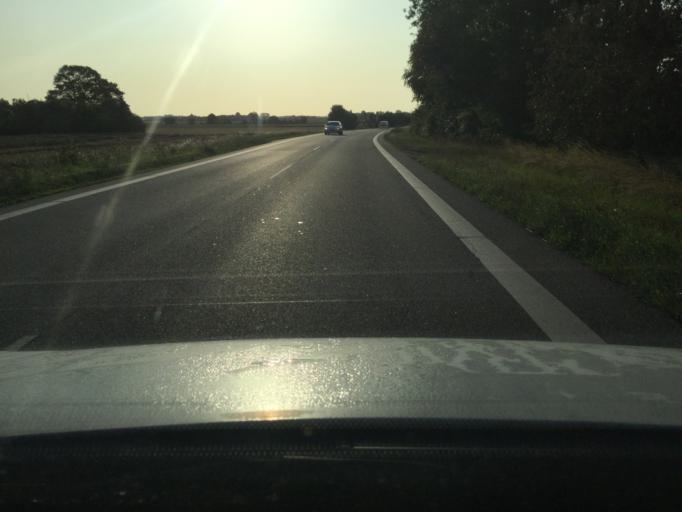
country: DK
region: Zealand
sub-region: Lolland Kommune
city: Nakskov
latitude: 54.8094
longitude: 11.2170
